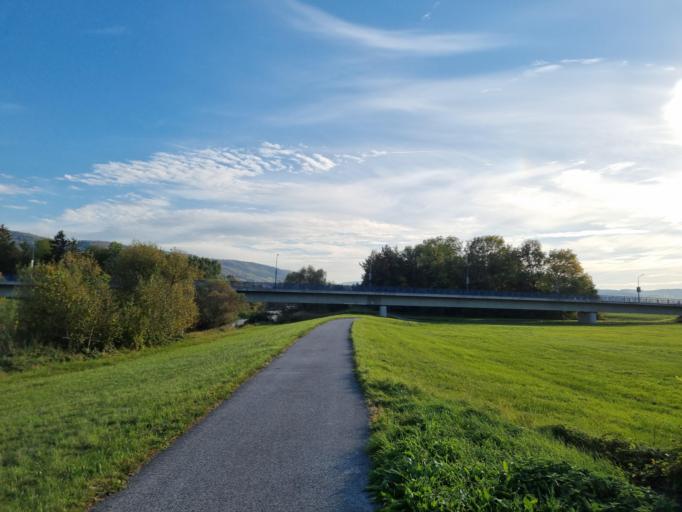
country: AT
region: Lower Austria
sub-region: Politischer Bezirk Sankt Polten
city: Wilhelmsburg
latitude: 48.1325
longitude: 15.6310
